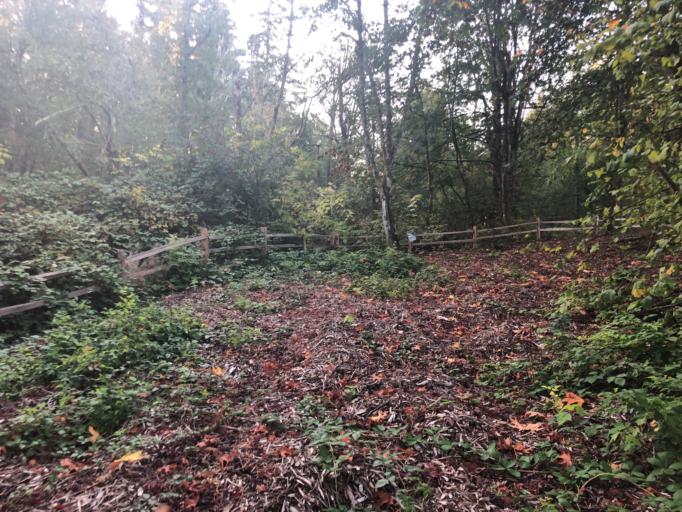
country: US
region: Washington
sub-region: King County
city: East Hill-Meridian
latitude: 47.3878
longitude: -122.1504
